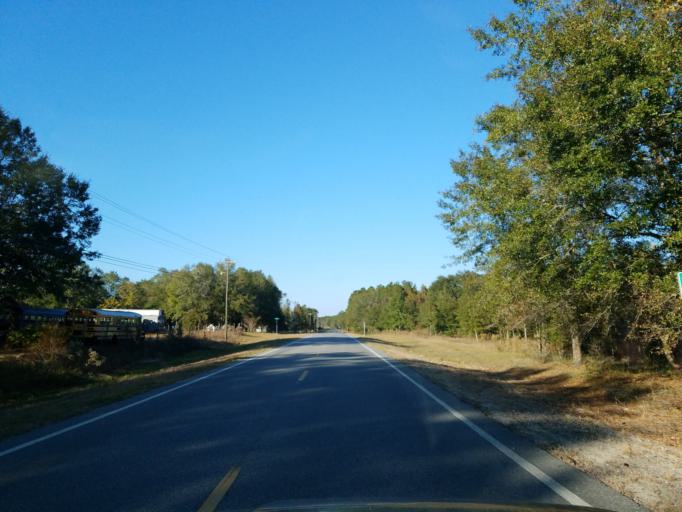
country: US
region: Georgia
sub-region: Echols County
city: Statenville
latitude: 30.7015
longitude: -83.0621
